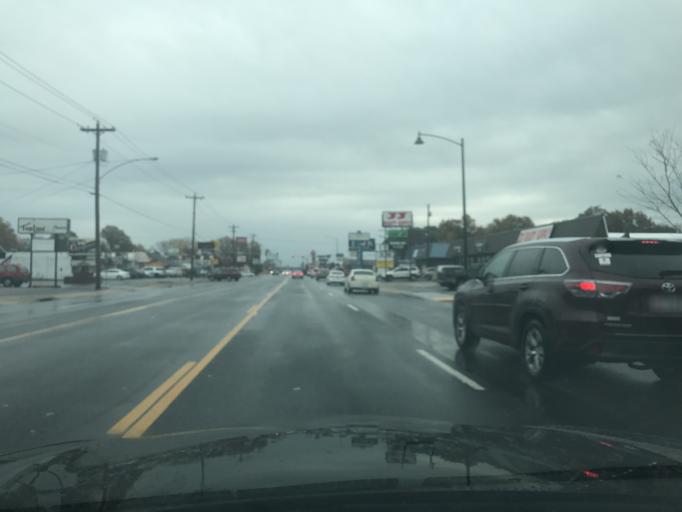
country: US
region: Arkansas
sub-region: Faulkner County
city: Conway
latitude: 35.0917
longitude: -92.4341
